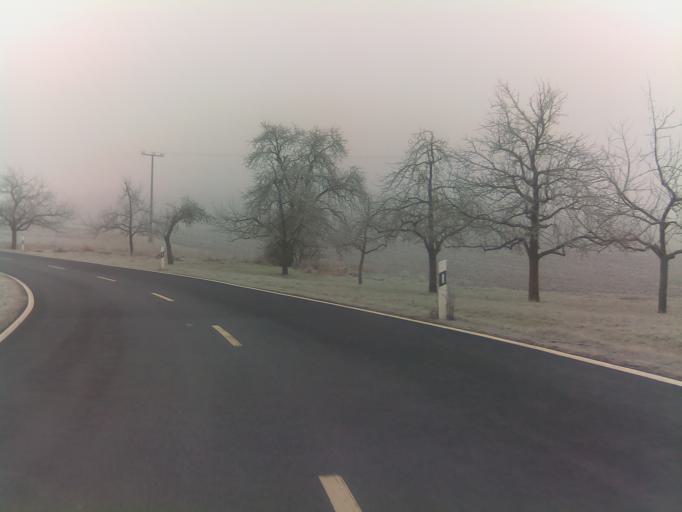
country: DE
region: Bavaria
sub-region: Regierungsbezirk Unterfranken
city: Donnersdorf
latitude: 49.9568
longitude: 10.4259
